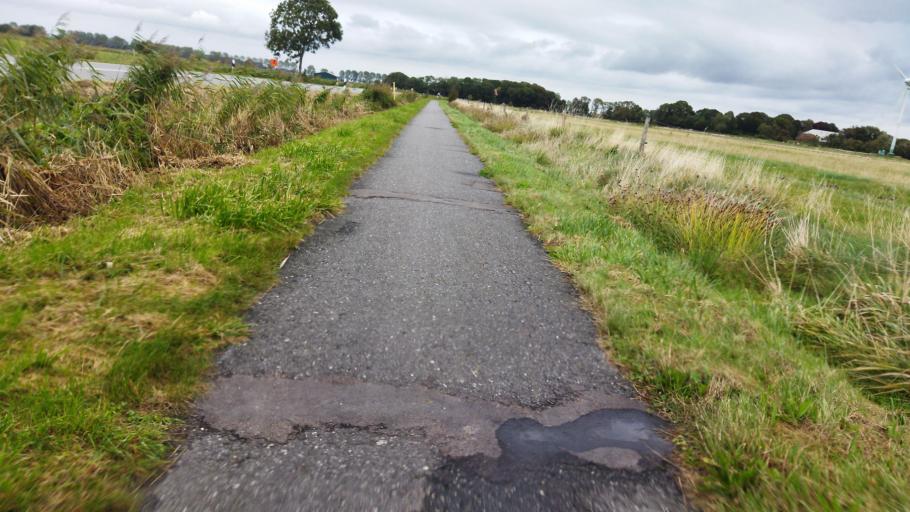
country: DE
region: Lower Saxony
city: Wirdum
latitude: 53.4844
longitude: 7.1311
